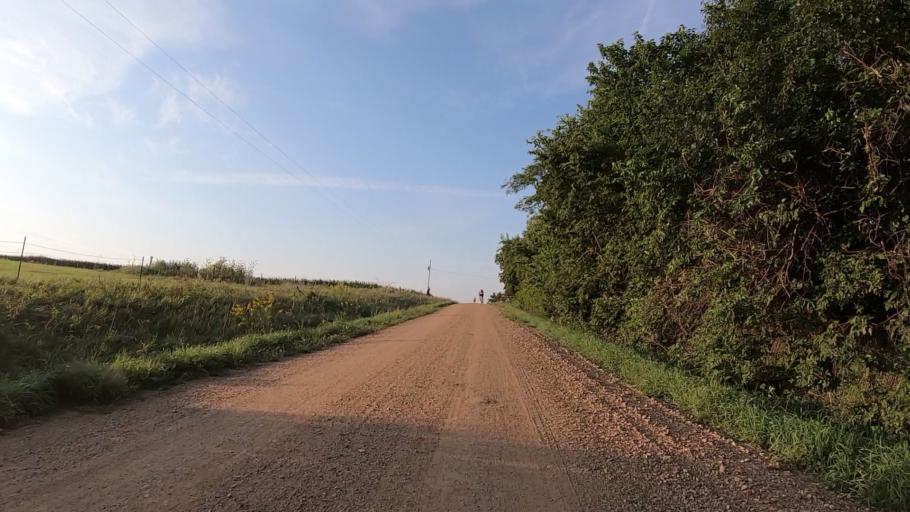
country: US
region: Kansas
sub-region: Marshall County
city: Blue Rapids
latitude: 39.7690
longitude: -96.7509
